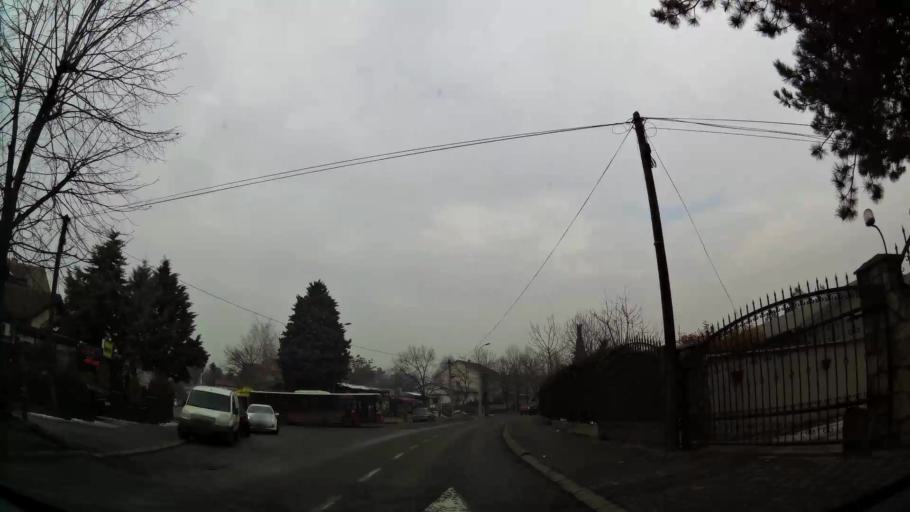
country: MK
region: Cair
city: Cair
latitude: 42.0144
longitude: 21.4567
